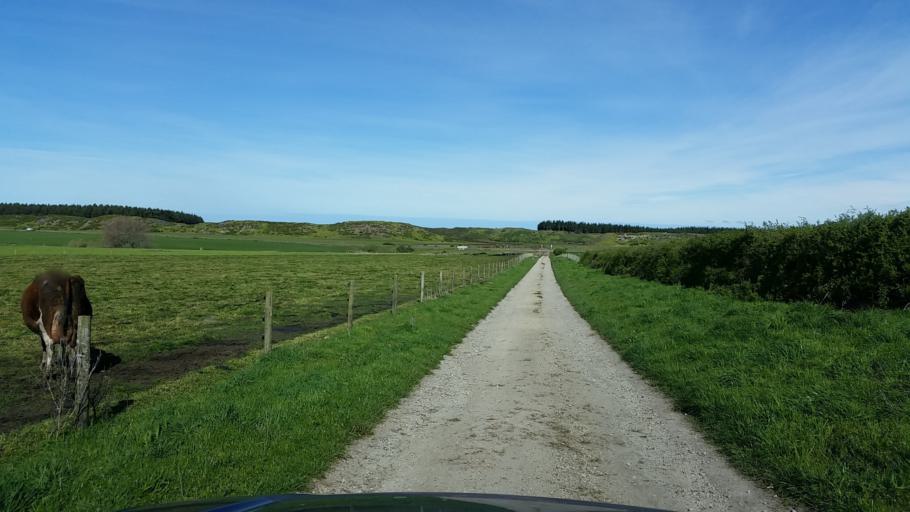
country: NZ
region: Taranaki
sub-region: South Taranaki District
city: Patea
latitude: -39.8212
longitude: 174.7718
